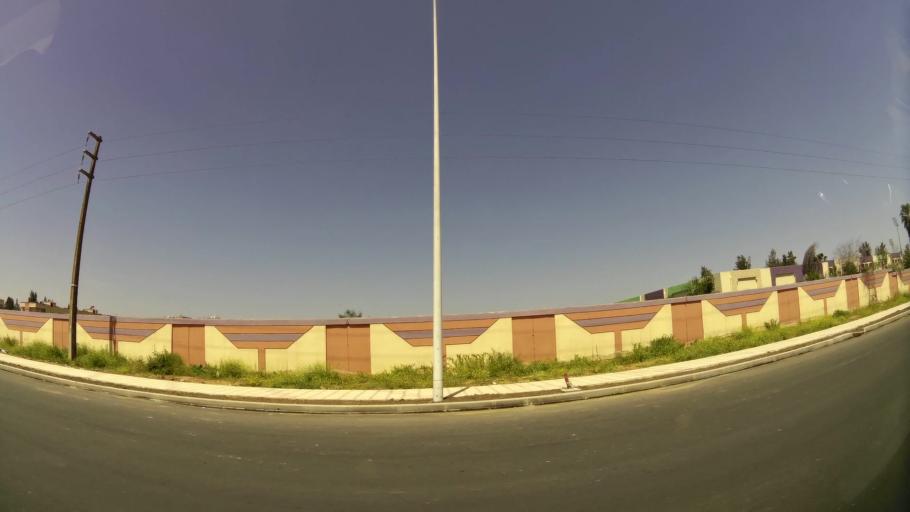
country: MA
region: Rabat-Sale-Zemmour-Zaer
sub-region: Khemisset
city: Khemisset
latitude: 33.8149
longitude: -6.0751
